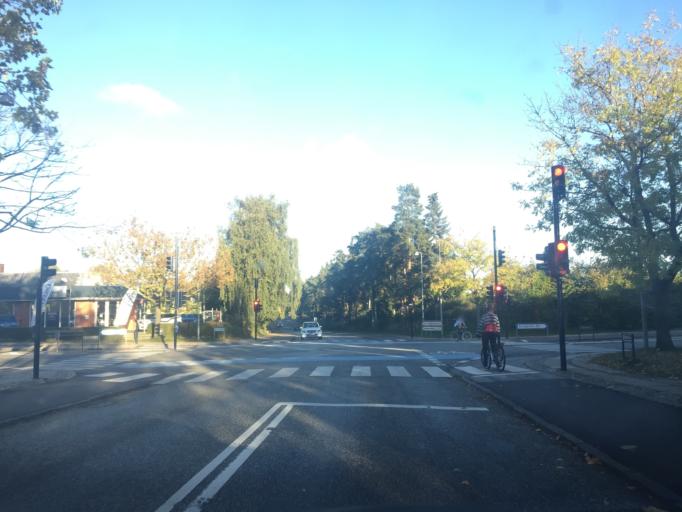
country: DK
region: Capital Region
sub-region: Rudersdal Kommune
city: Holte
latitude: 55.7885
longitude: 12.4731
